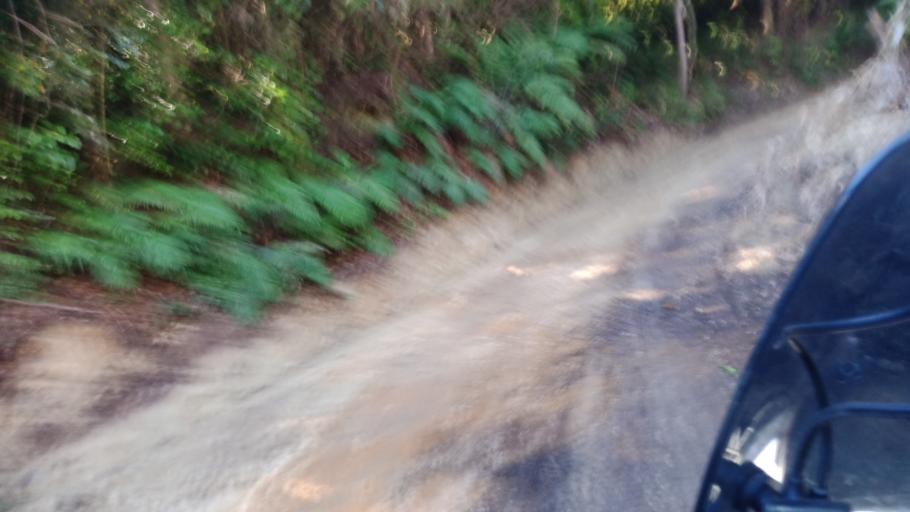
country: NZ
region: Hawke's Bay
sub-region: Wairoa District
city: Wairoa
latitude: -38.9975
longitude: 177.0690
